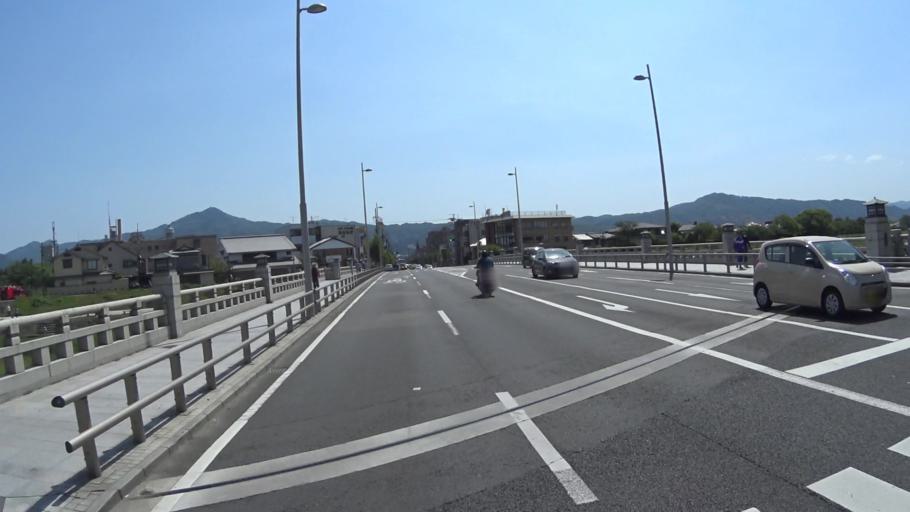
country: JP
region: Kyoto
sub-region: Kyoto-shi
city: Kamigyo-ku
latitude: 35.0439
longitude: 135.7616
